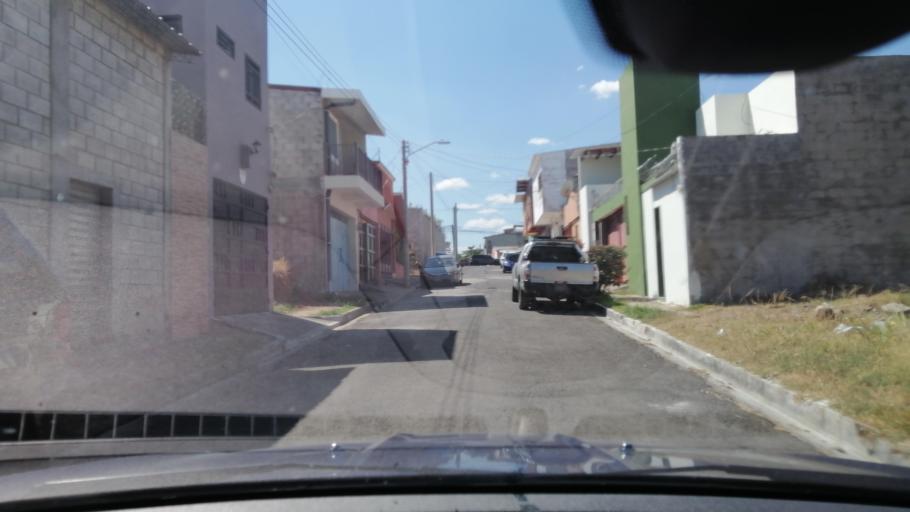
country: SV
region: Santa Ana
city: Santa Ana
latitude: 13.9655
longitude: -89.5737
